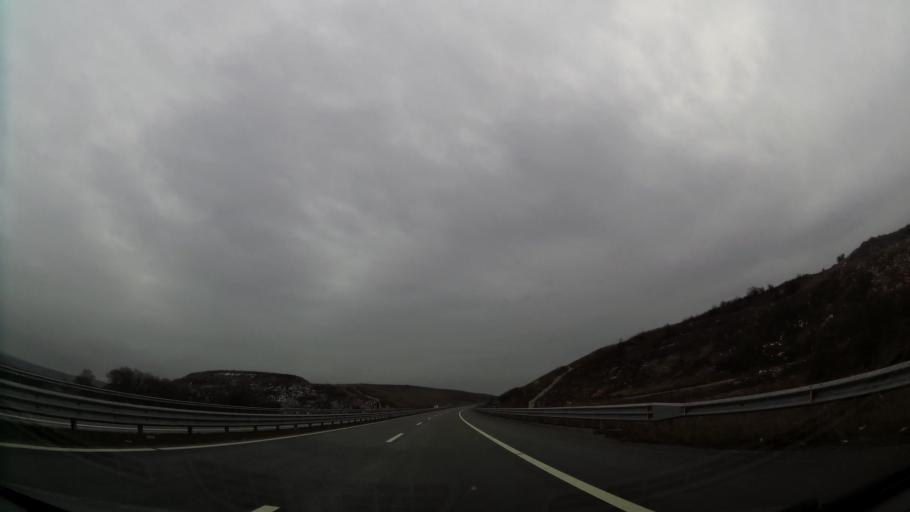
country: XK
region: Ferizaj
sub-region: Komuna e Ferizajt
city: Ferizaj
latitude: 42.4387
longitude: 21.2000
